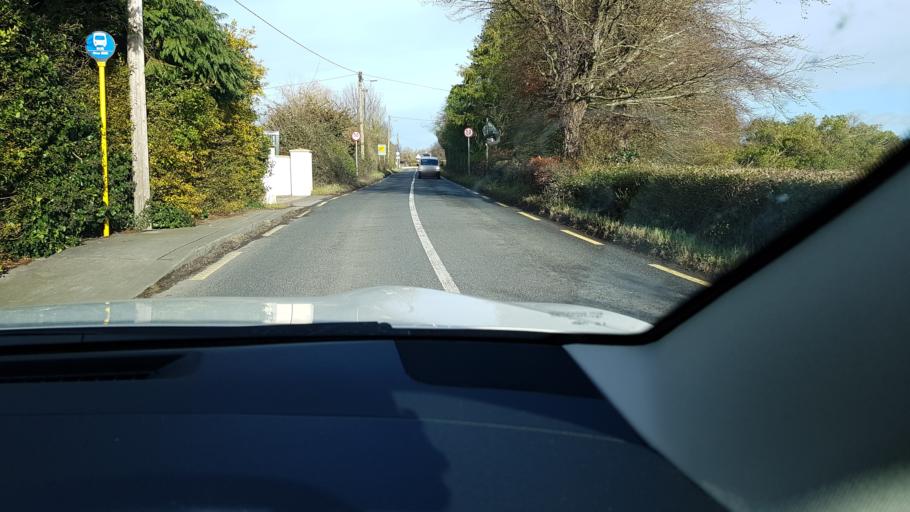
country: IE
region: Leinster
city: Lucan
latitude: 53.3710
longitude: -6.4563
